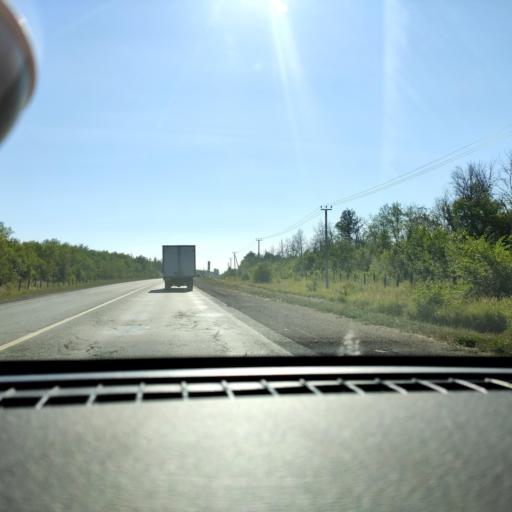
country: RU
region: Samara
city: Chapayevsk
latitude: 52.9953
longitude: 49.8029
